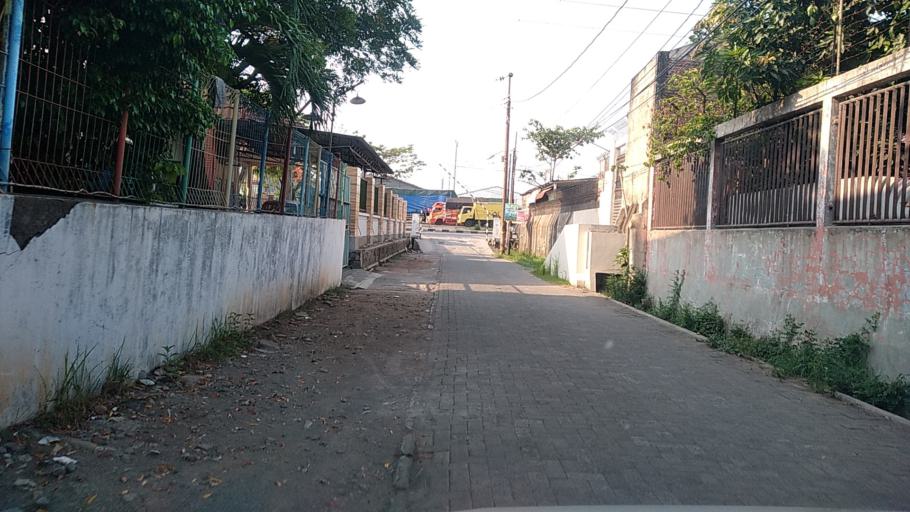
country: ID
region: Central Java
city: Semarang
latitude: -6.9542
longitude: 110.4070
